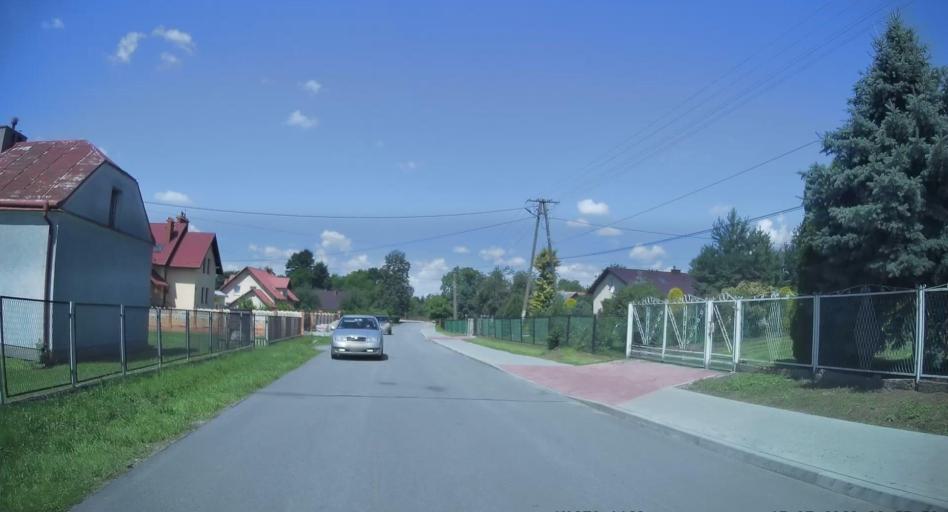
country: PL
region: Subcarpathian Voivodeship
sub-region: Powiat jaroslawski
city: Sosnica
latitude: 49.8640
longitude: 22.8788
